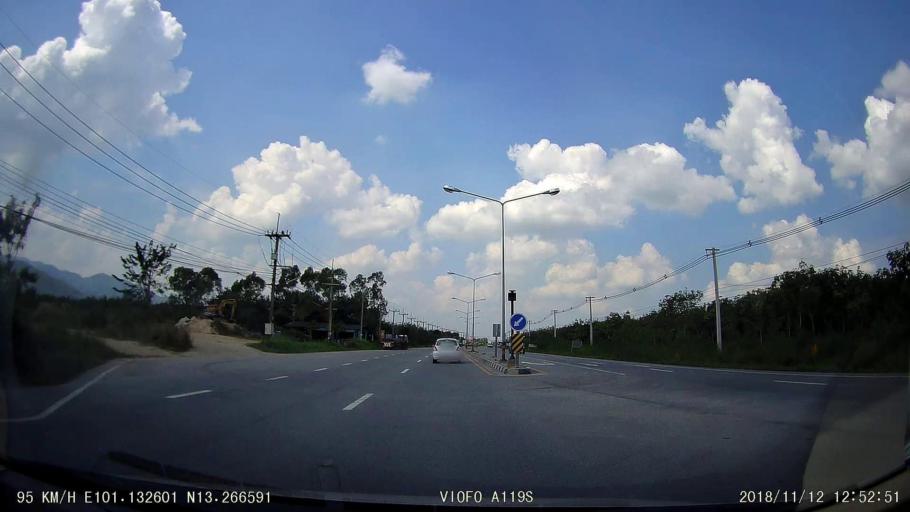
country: TH
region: Chon Buri
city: Ban Bueng
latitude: 13.2668
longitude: 101.1325
